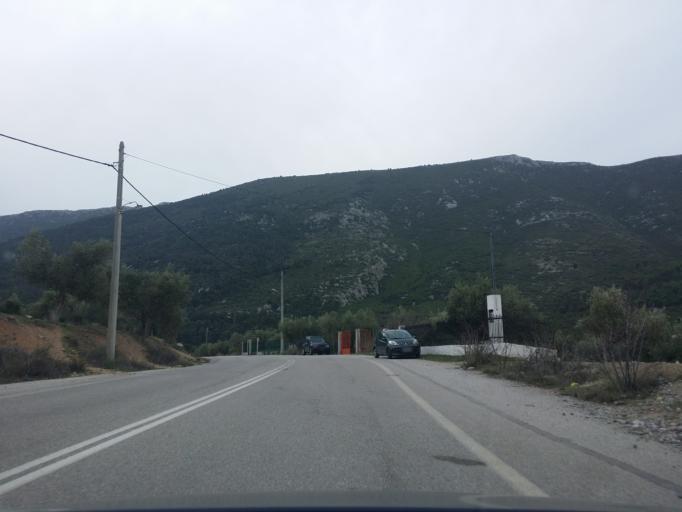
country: GR
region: Attica
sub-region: Nomarchia Dytikis Attikis
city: Vilia
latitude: 38.1462
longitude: 23.2511
